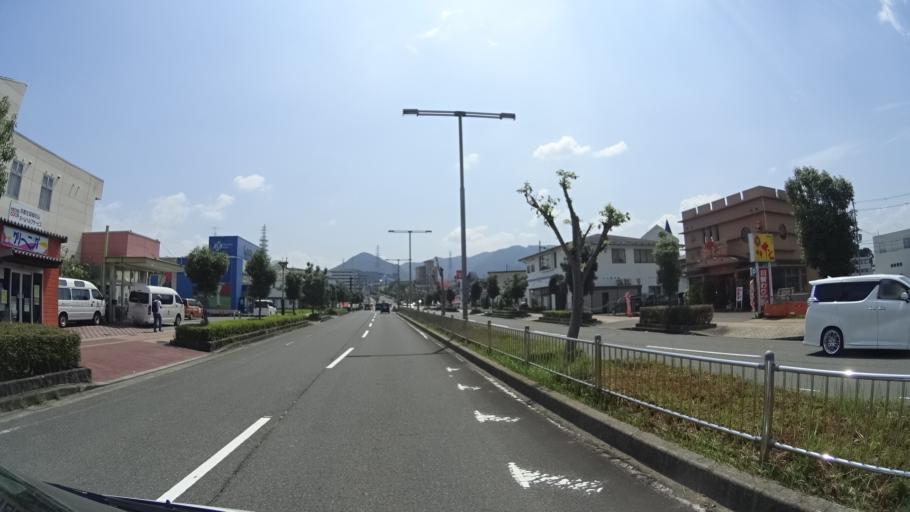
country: JP
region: Kyoto
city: Fukuchiyama
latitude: 35.2945
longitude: 135.1180
